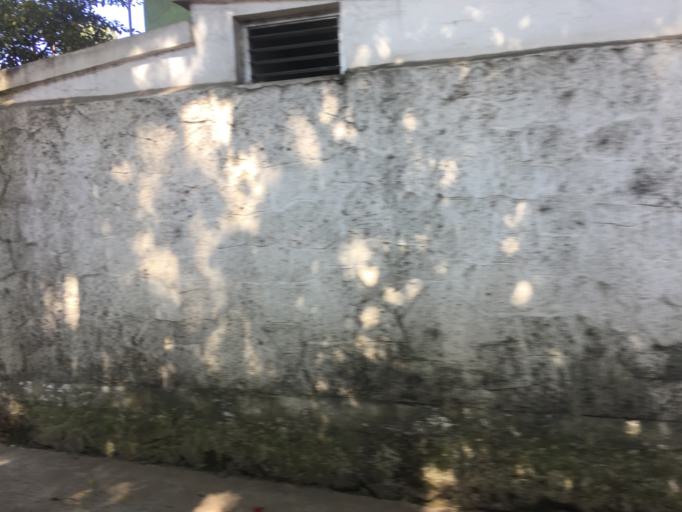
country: MX
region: Veracruz
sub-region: Xalapa
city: Xalapa de Enriquez
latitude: 19.5350
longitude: -96.9106
